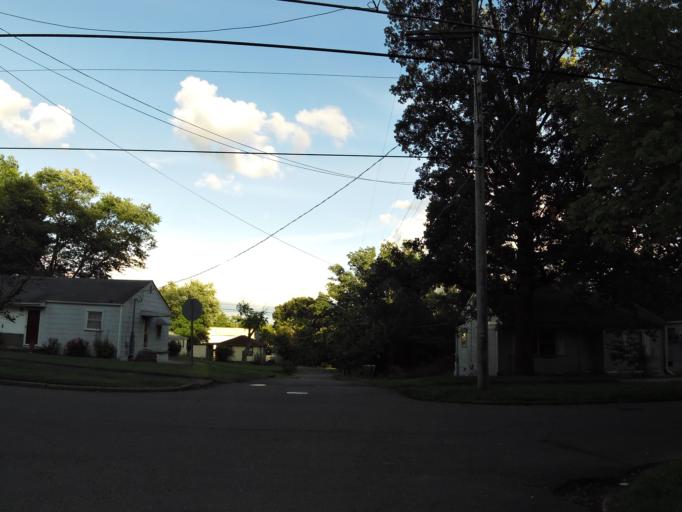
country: US
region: Tennessee
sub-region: Knox County
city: Knoxville
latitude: 36.0050
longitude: -83.9337
